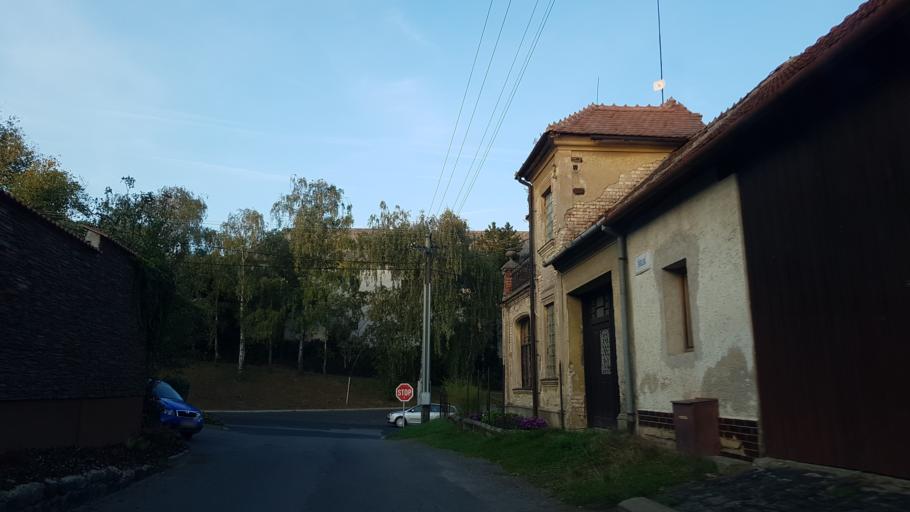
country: CZ
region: Zlin
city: Polesovice
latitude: 49.0297
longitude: 17.3481
